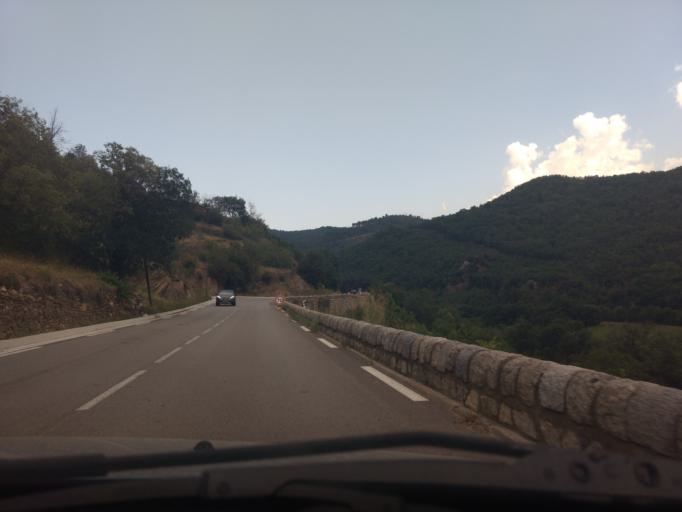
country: FR
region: Languedoc-Roussillon
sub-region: Departement des Pyrenees-Orientales
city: Vernet-les-Bains
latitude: 42.5690
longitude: 2.3268
